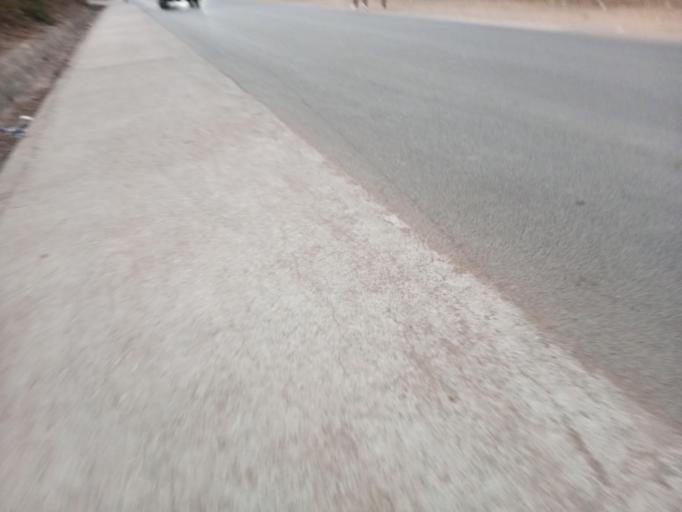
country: ZM
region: Lusaka
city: Lusaka
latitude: -15.4001
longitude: 28.2952
